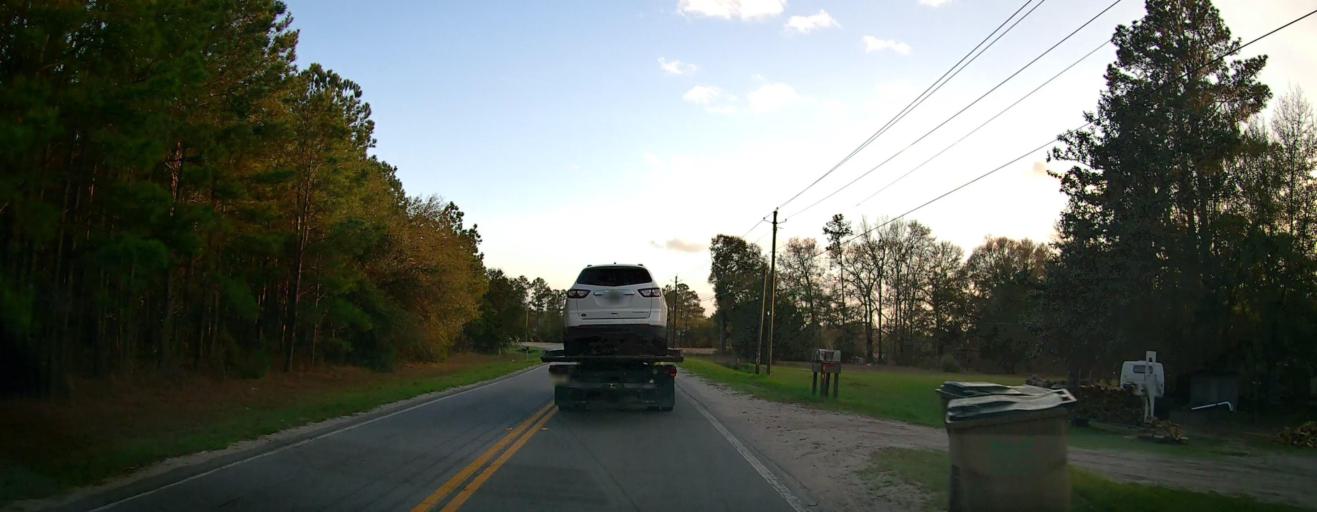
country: US
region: Georgia
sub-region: Chatham County
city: Bloomingdale
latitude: 32.1440
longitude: -81.3905
